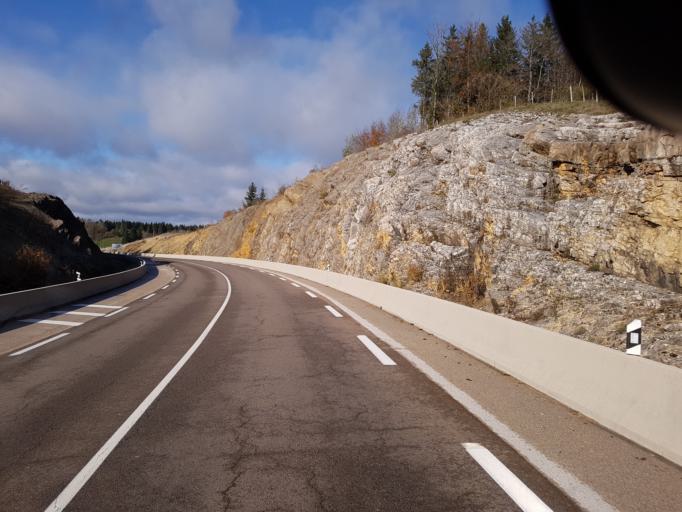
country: FR
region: Franche-Comte
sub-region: Departement du Jura
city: Morbier
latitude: 46.5827
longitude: 5.9581
